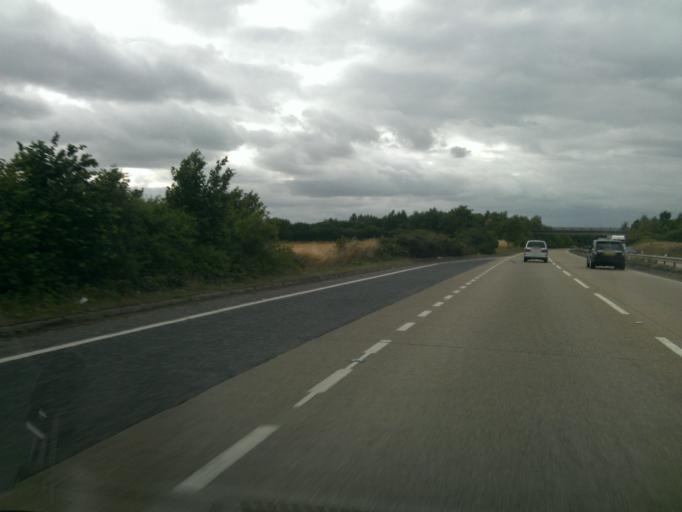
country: GB
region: England
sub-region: Essex
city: Wivenhoe
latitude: 51.9026
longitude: 0.9754
